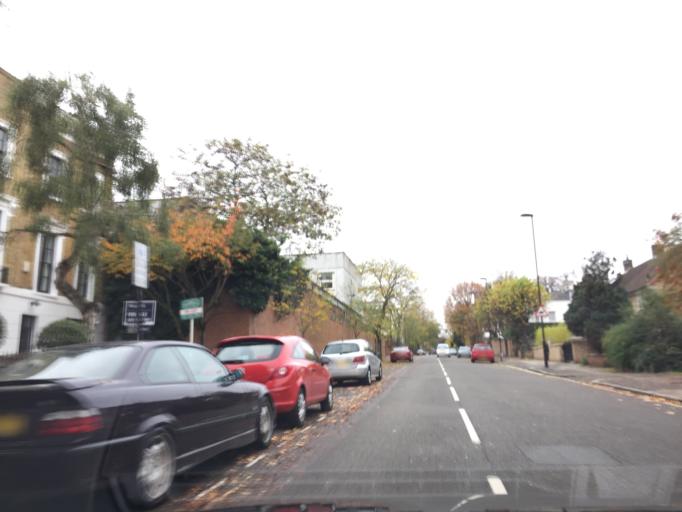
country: GB
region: England
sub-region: Greater London
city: Belsize Park
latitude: 51.5360
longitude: -0.1715
